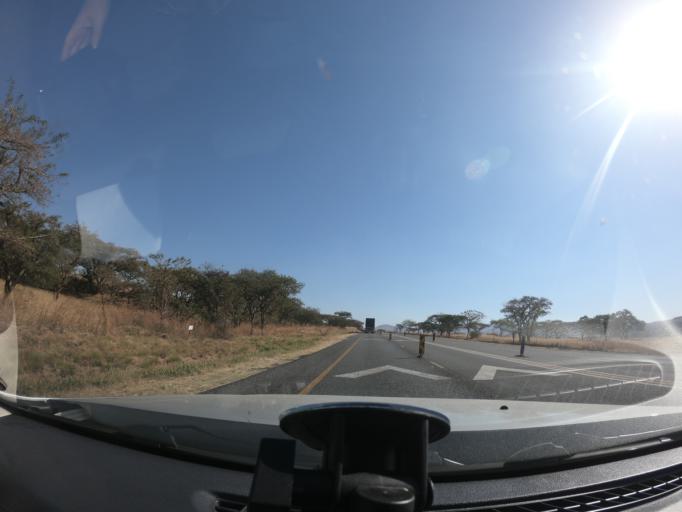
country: ZA
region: KwaZulu-Natal
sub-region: uThukela District Municipality
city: Ladysmith
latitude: -28.4372
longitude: 29.4860
